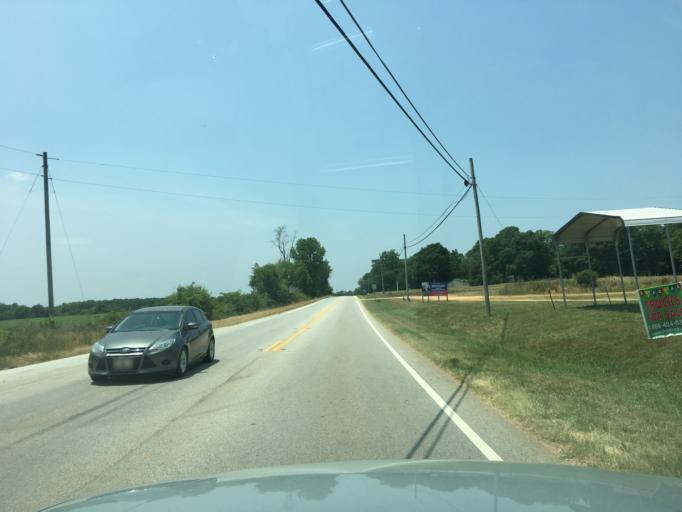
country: US
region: Georgia
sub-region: Hart County
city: Royston
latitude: 34.2884
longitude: -83.0903
